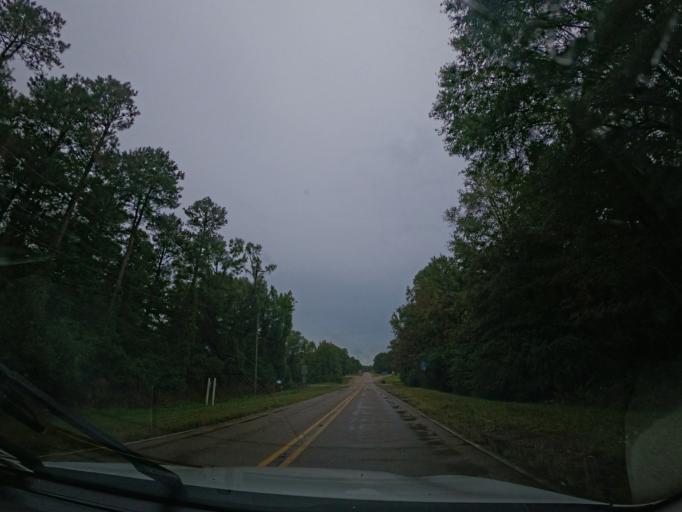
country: US
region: Louisiana
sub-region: Bienville Parish
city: Arcadia
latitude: 32.5591
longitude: -93.0542
